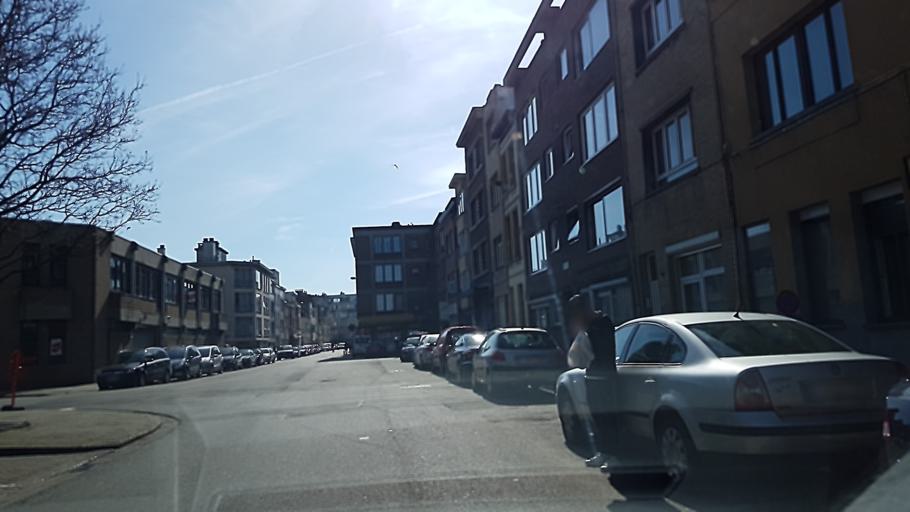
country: BE
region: Flanders
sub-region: Provincie Antwerpen
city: Antwerpen
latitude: 51.2253
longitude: 4.4256
